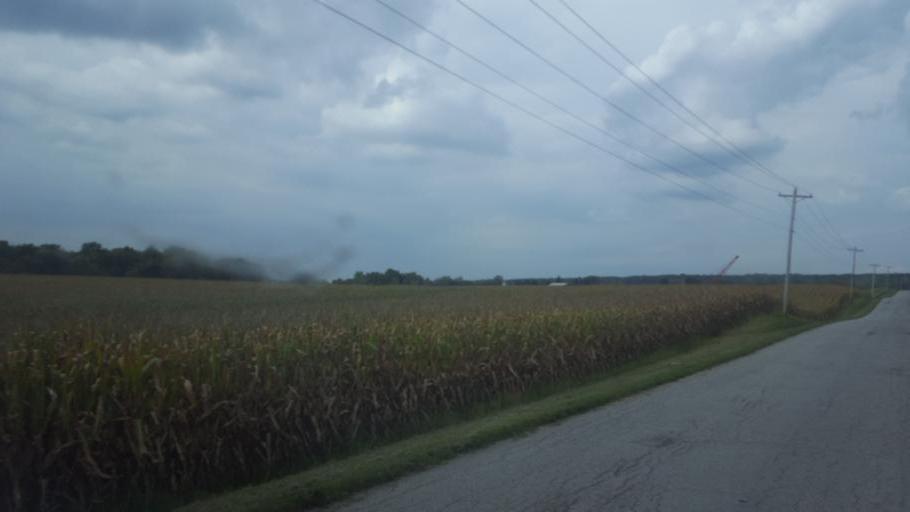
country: US
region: Ohio
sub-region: Knox County
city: Fredericktown
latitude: 40.4618
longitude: -82.6563
